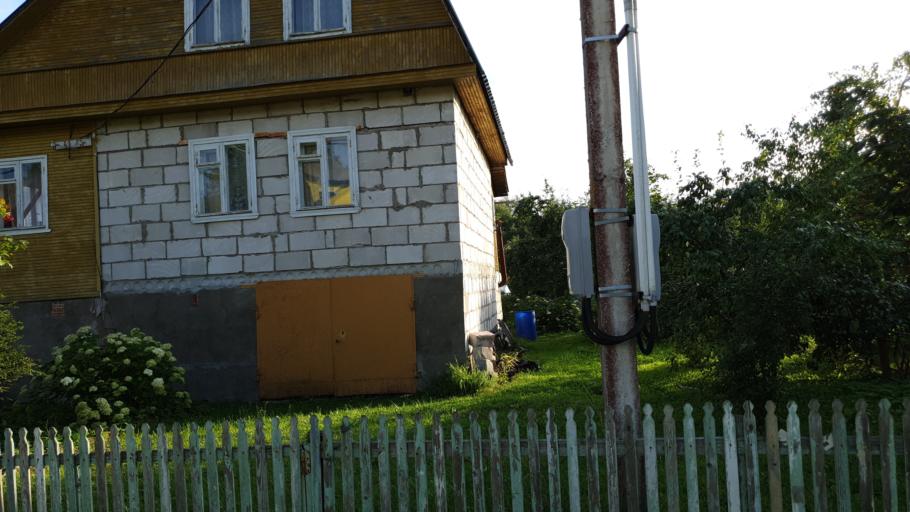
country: RU
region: Leningrad
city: Ivangorod
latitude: 59.4238
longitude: 28.3329
